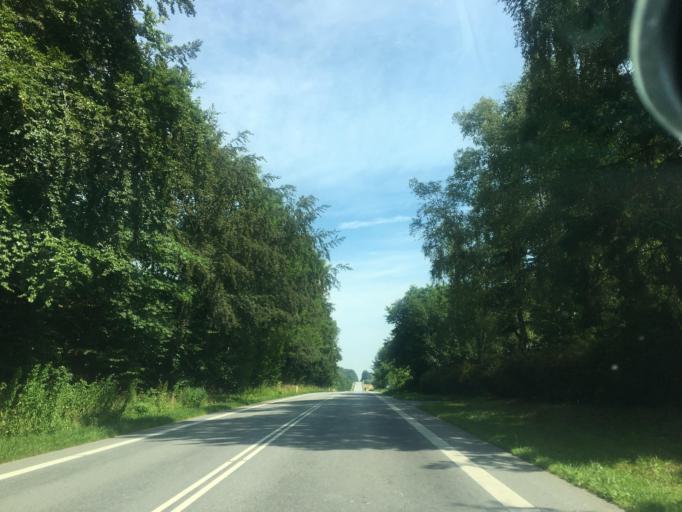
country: DK
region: Zealand
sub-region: Faxe Kommune
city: Ronnede
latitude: 55.2127
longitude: 11.9947
